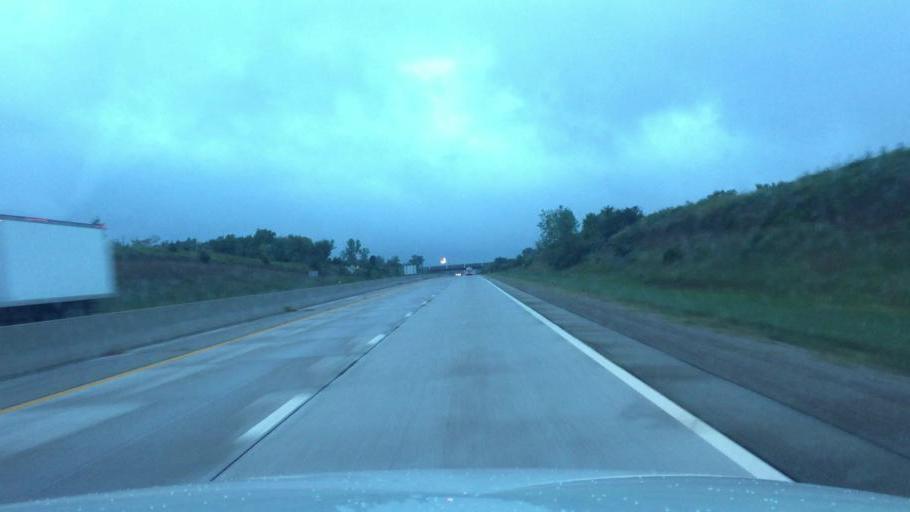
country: US
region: Kansas
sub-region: Neosho County
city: Chanute
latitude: 37.6699
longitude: -95.4796
